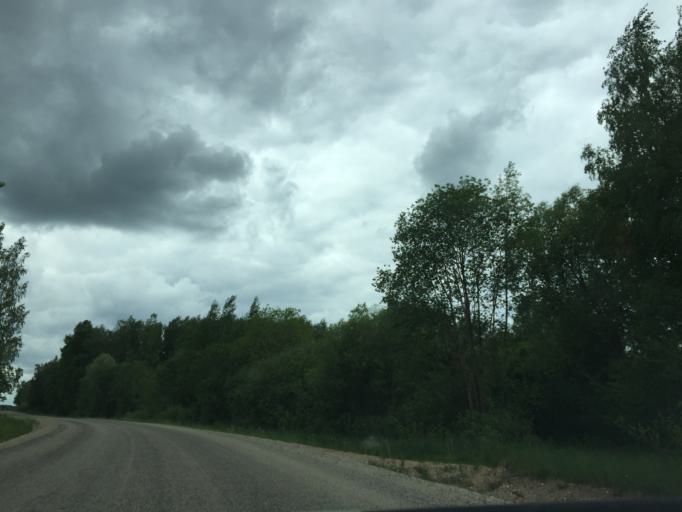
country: LV
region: Dagda
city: Dagda
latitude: 56.0689
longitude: 27.5585
